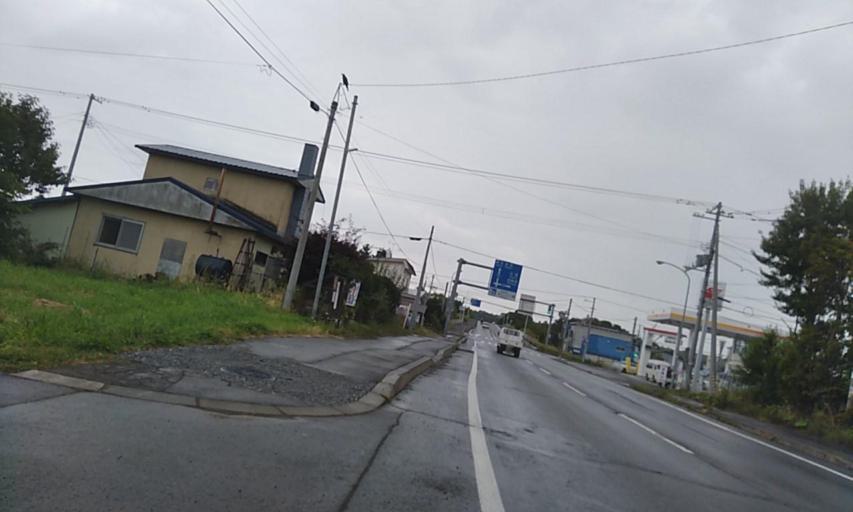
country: JP
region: Hokkaido
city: Mombetsu
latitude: 44.4743
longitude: 143.1214
